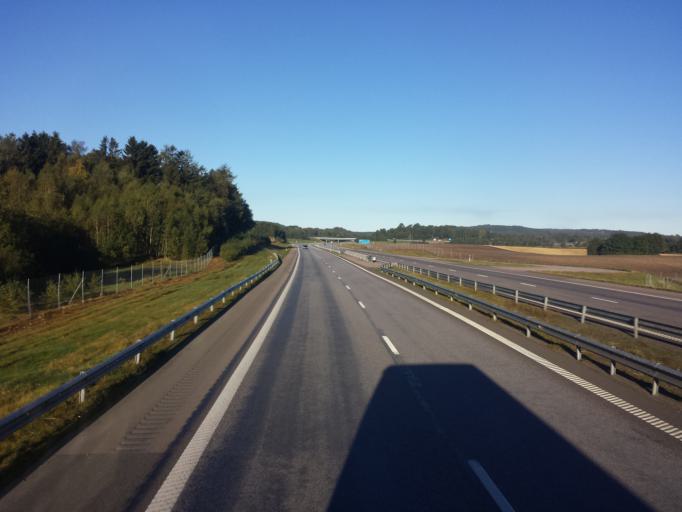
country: SE
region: Halland
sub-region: Halmstads Kommun
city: Getinge
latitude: 56.8045
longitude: 12.7522
